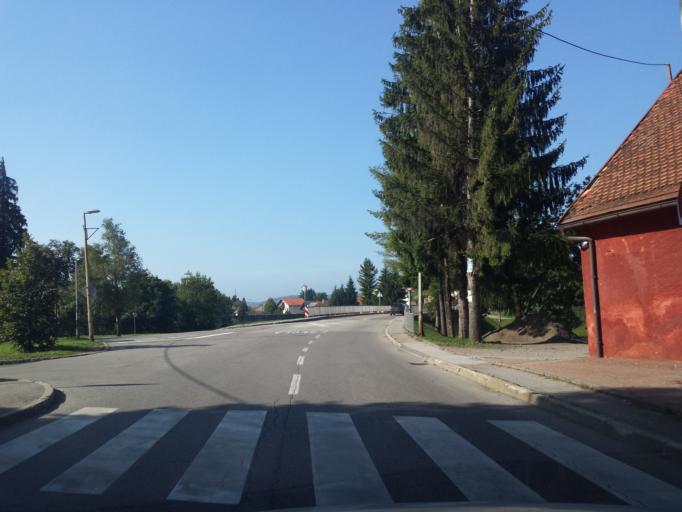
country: HR
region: Karlovacka
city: Ostarije
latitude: 45.2236
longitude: 15.2752
